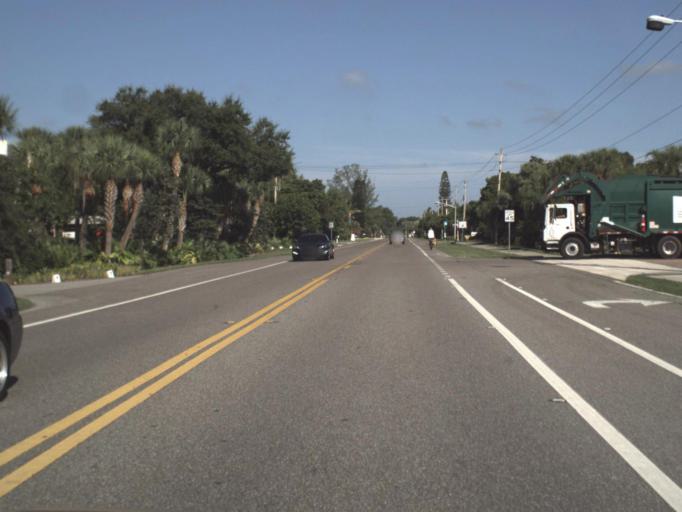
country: US
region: Florida
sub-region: Manatee County
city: Longboat Key
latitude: 27.4165
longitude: -82.6630
